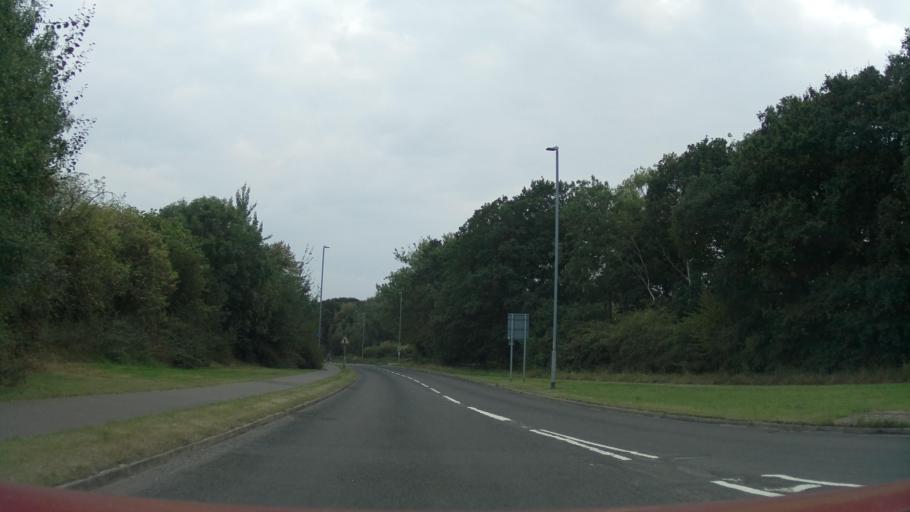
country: GB
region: England
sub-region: Nottinghamshire
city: South Collingham
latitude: 53.1485
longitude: -0.6693
